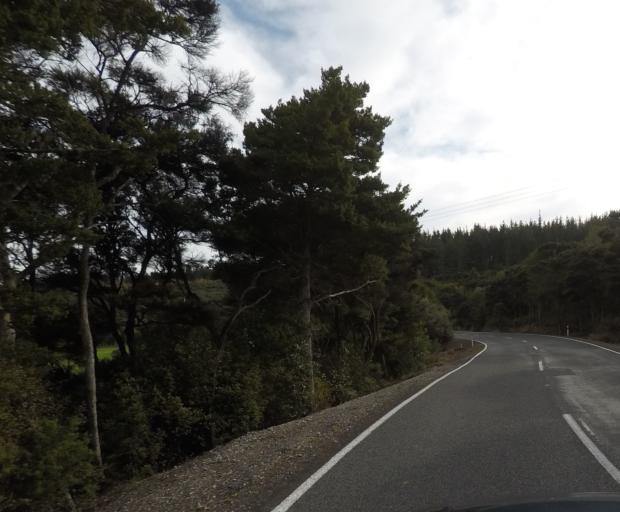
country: NZ
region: Northland
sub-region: Whangarei
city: Ruakaka
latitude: -36.0542
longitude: 174.5502
